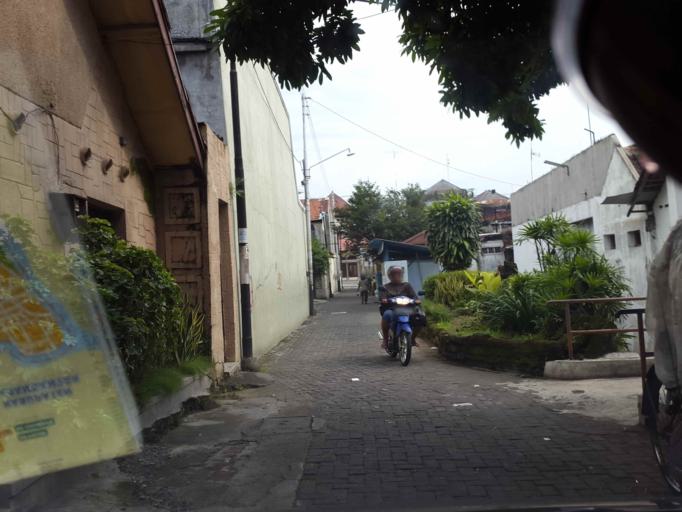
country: ID
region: Central Java
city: Surakarta
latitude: -7.5693
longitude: 110.8354
